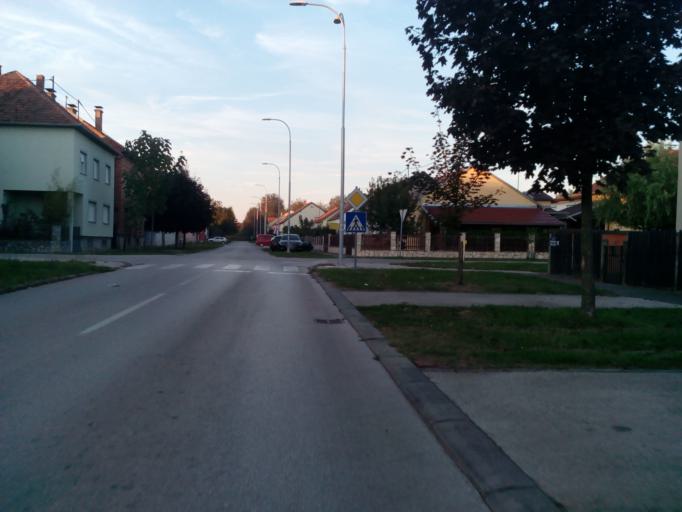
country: HR
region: Vukovarsko-Srijemska
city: Vinkovci
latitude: 45.2974
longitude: 18.8169
